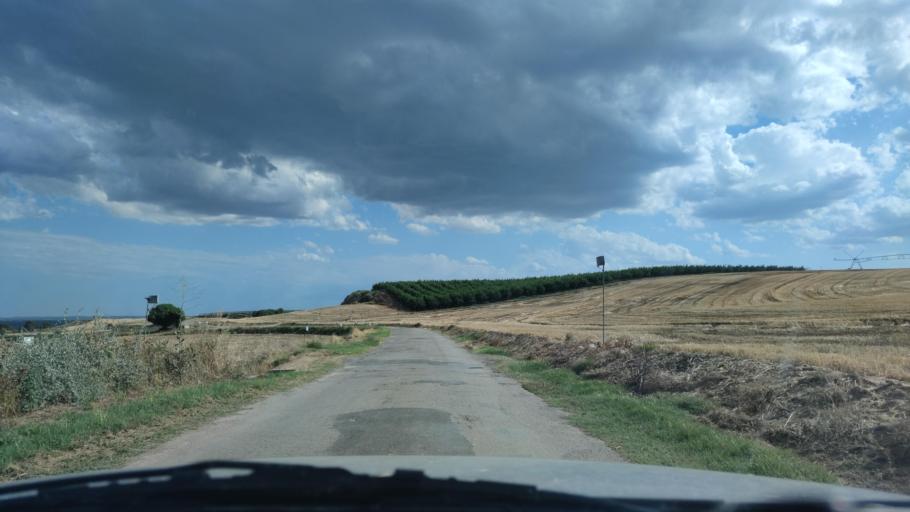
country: ES
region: Catalonia
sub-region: Provincia de Lleida
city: Alcarras
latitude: 41.5957
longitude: 0.5417
